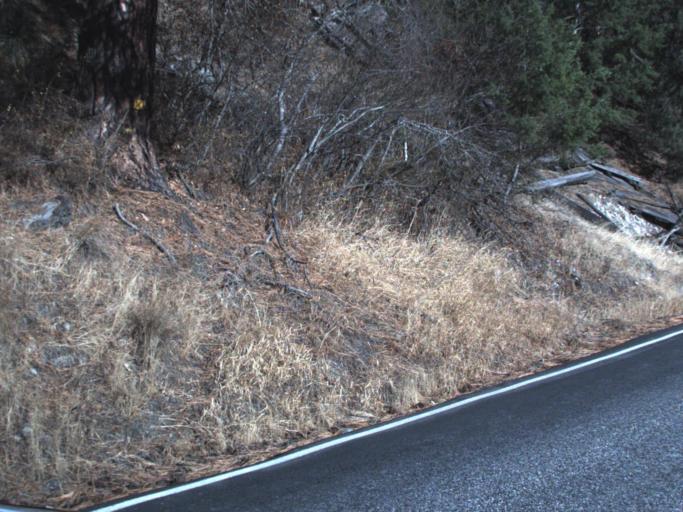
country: US
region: Washington
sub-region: Ferry County
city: Republic
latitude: 48.5753
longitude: -118.7443
